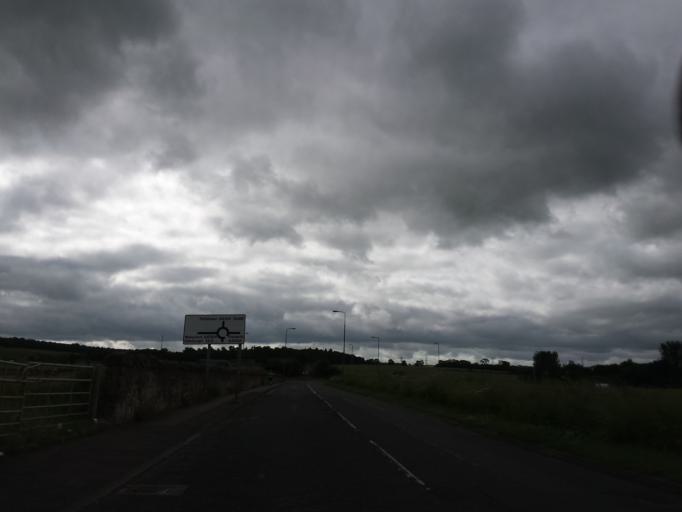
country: GB
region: Scotland
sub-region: East Lothian
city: Musselburgh
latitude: 55.9246
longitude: -3.0346
